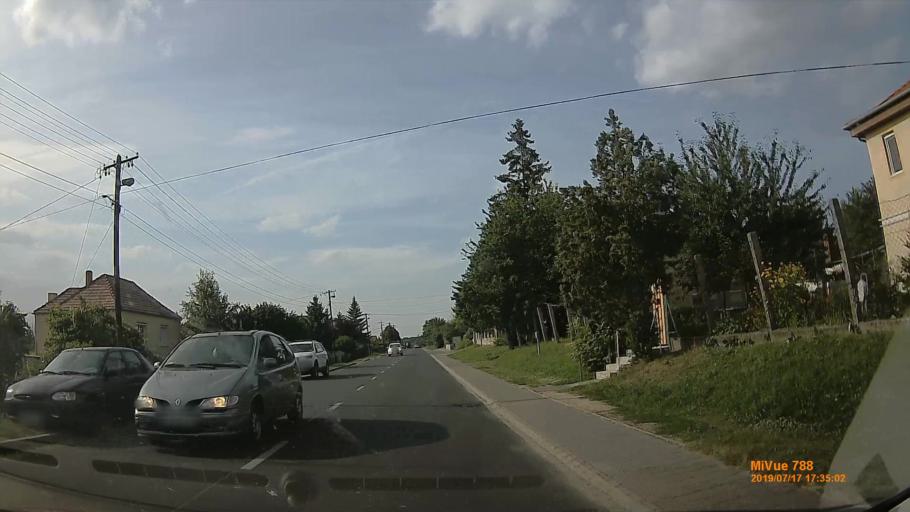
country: HU
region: Veszprem
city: Ajka
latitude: 47.0614
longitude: 17.5535
